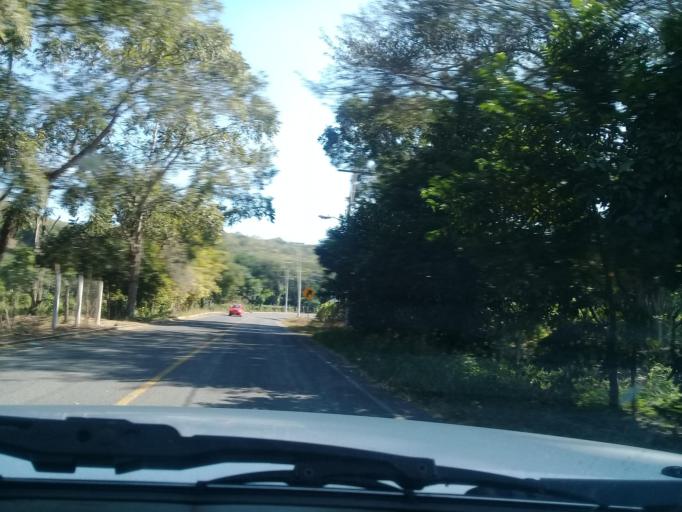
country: MX
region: Veracruz
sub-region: Emiliano Zapata
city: Plan del Rio
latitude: 19.4171
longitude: -96.6150
